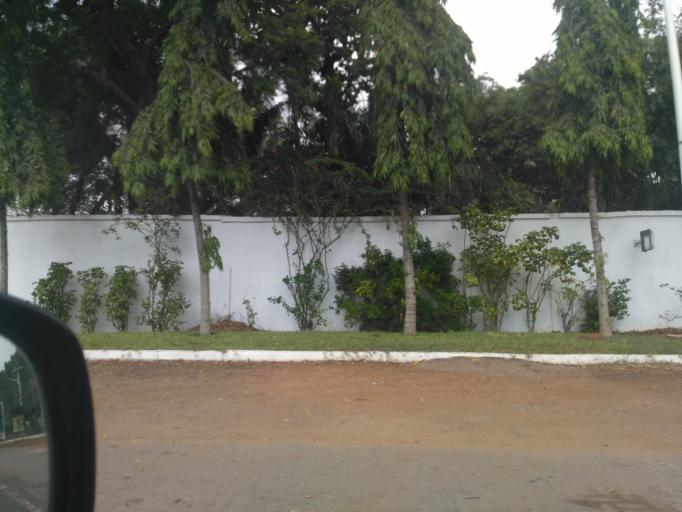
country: GH
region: Greater Accra
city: Accra
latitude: 5.5796
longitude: -0.1858
